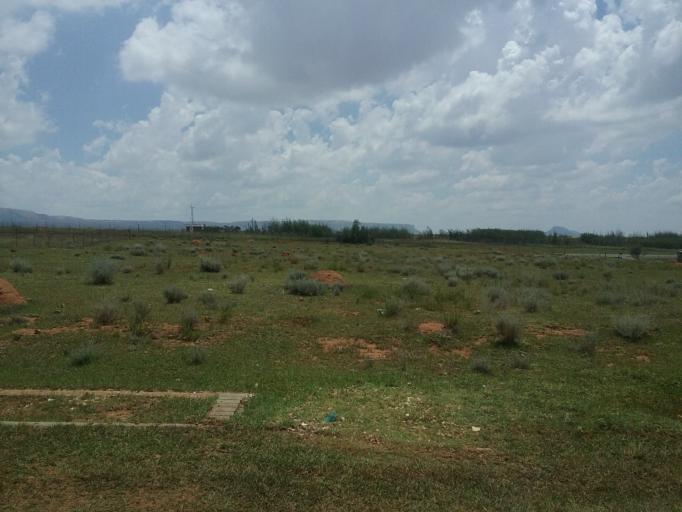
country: LS
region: Maseru
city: Maseru
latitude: -29.4493
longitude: 27.5623
